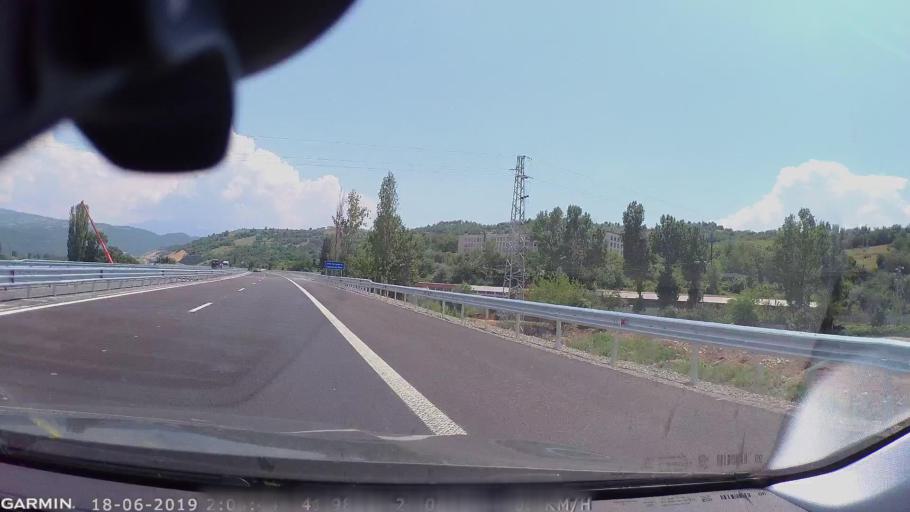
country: BG
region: Blagoevgrad
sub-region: Obshtina Blagoevgrad
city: Blagoevgrad
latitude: 41.9827
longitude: 23.0605
